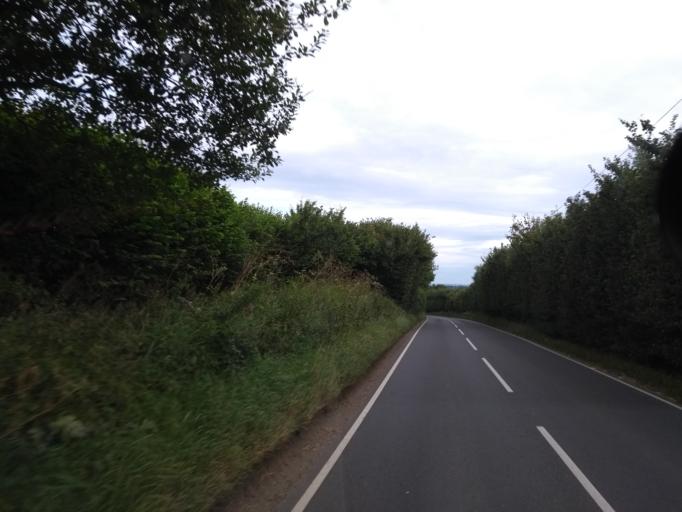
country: GB
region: England
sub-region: Somerset
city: Crewkerne
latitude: 50.8509
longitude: -2.7718
